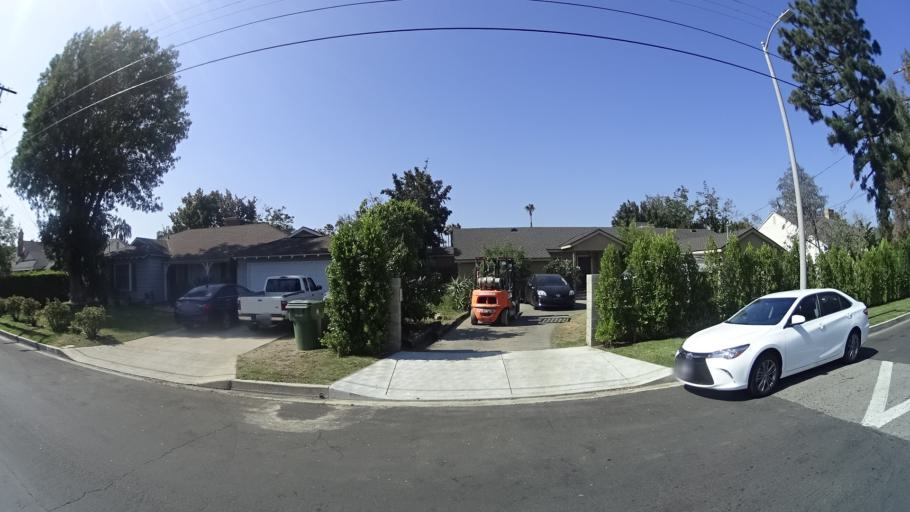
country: US
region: California
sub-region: Los Angeles County
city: Van Nuys
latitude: 34.1958
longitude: -118.4293
